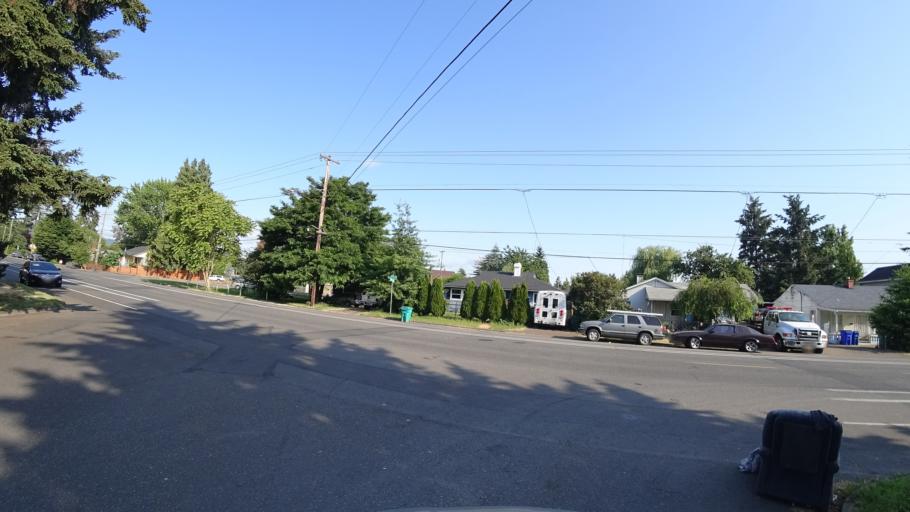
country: US
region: Oregon
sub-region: Washington County
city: West Haven
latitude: 45.5921
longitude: -122.7353
